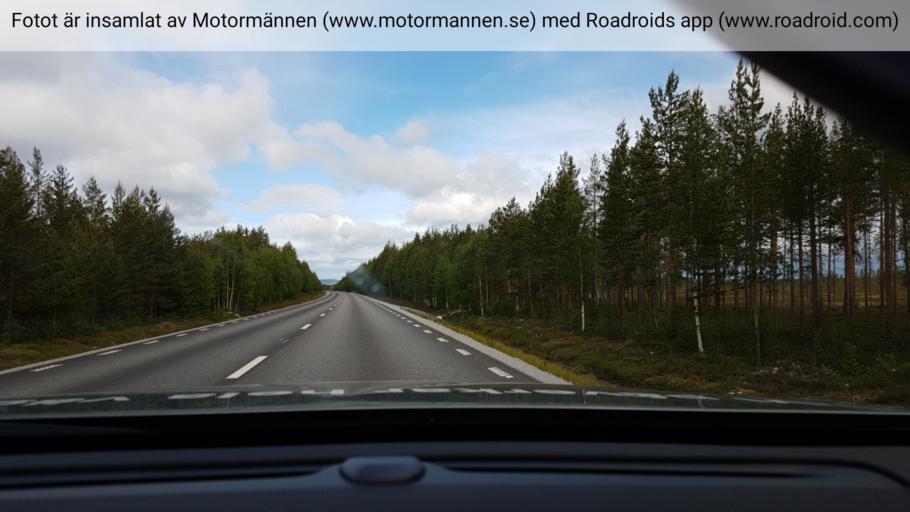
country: SE
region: Vaesternorrland
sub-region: OErnskoeldsviks Kommun
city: Bredbyn
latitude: 64.0976
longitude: 18.1715
